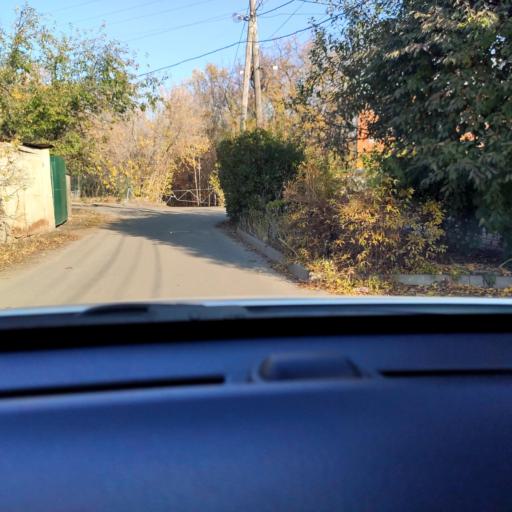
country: RU
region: Voronezj
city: Voronezh
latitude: 51.6974
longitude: 39.2141
